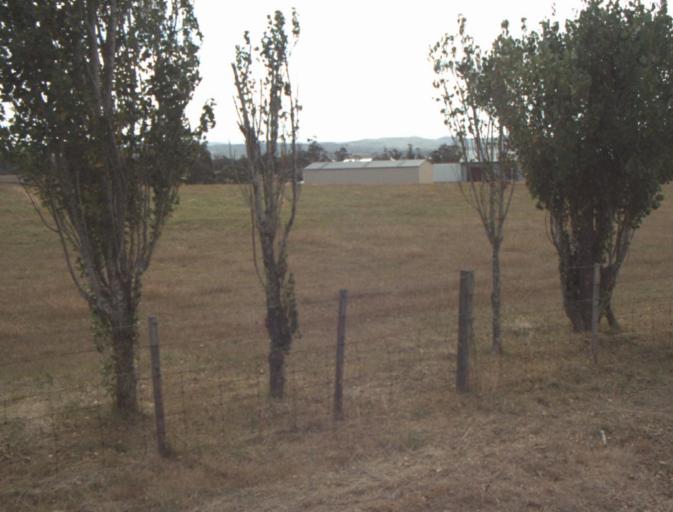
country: AU
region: Tasmania
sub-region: Launceston
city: Mayfield
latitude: -41.3028
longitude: 147.0350
